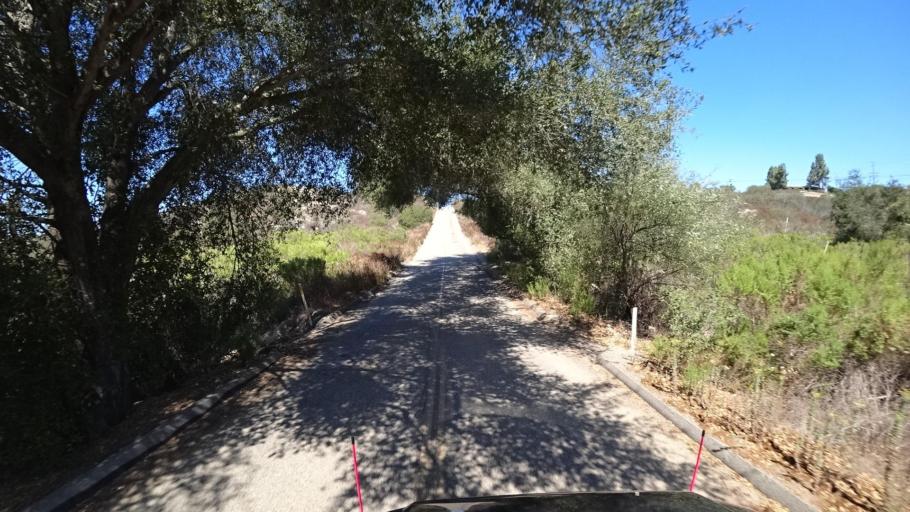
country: US
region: California
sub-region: San Diego County
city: Hidden Meadows
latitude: 33.2448
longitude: -117.0859
